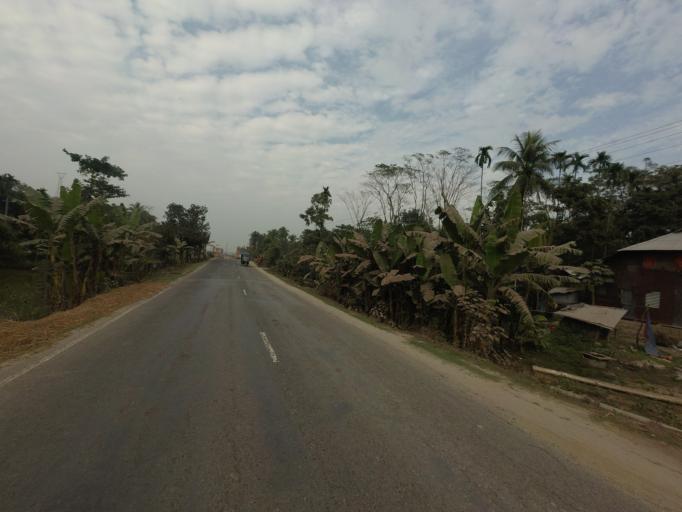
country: BD
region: Barisal
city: Nalchiti
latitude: 22.4562
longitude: 90.3407
